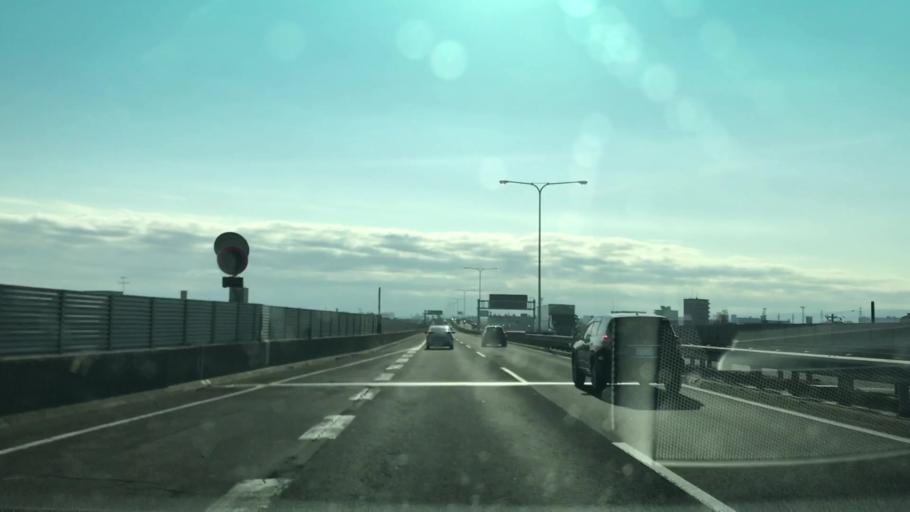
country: JP
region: Hokkaido
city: Sapporo
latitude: 43.0568
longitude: 141.4271
